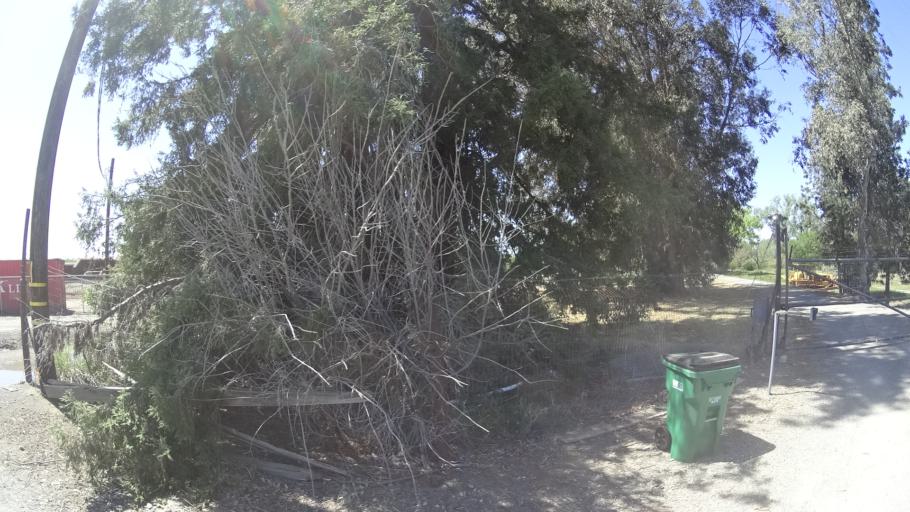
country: US
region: California
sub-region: Glenn County
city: Orland
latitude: 39.7572
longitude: -122.1598
